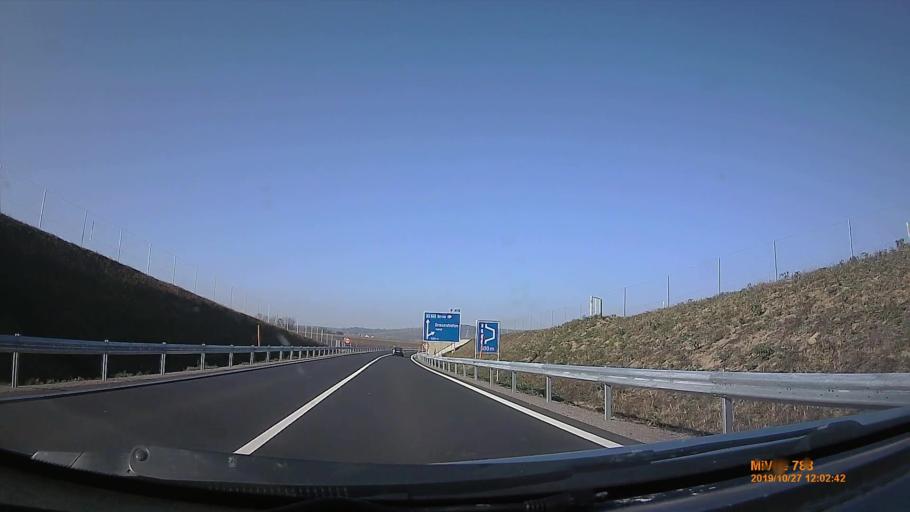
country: AT
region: Lower Austria
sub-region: Politischer Bezirk Mistelbach
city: Drasenhofen
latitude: 48.7365
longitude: 16.6473
